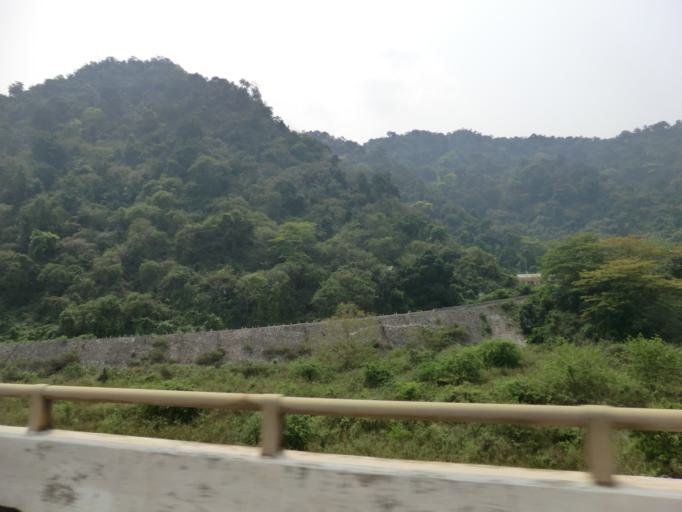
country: VN
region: Hoa Binh
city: Thi Tran Hang Tram
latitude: 20.3963
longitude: 105.5246
